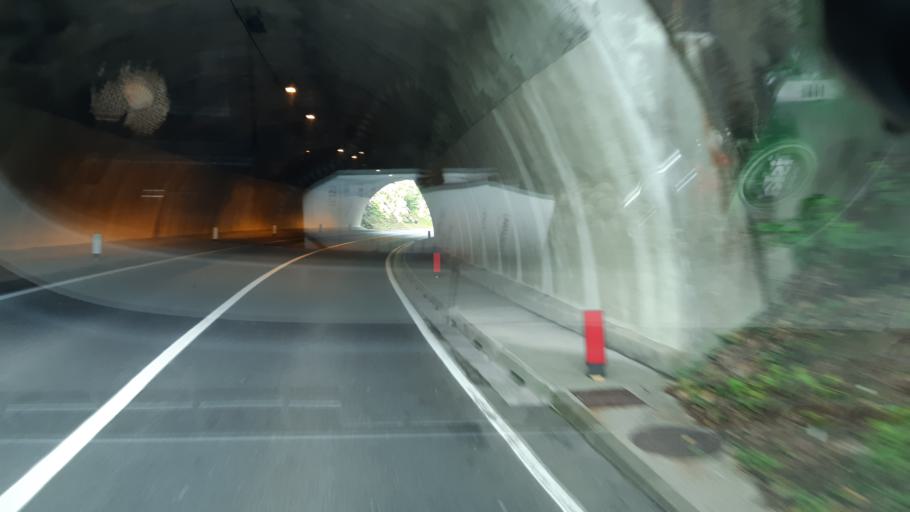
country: SI
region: Trzic
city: Trzic
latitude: 46.3686
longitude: 14.3058
